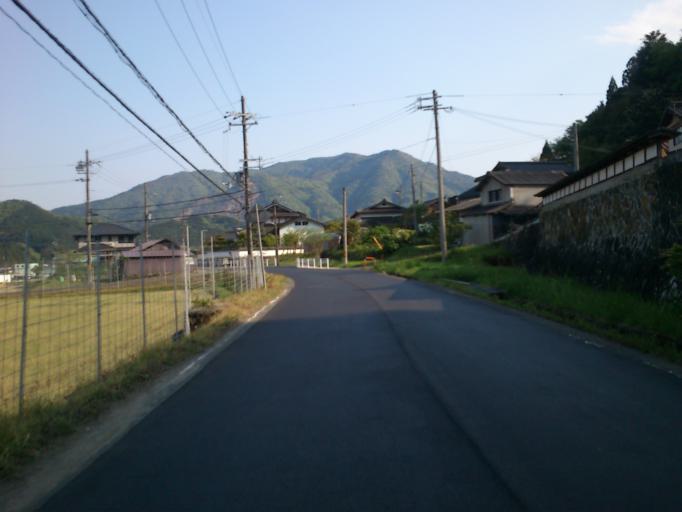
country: JP
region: Kyoto
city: Fukuchiyama
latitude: 35.2981
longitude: 135.0784
